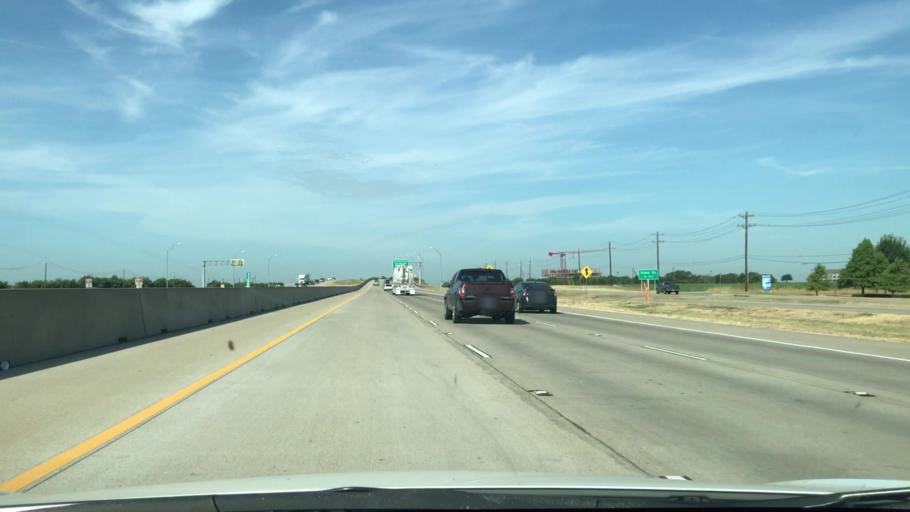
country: US
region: Texas
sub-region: Collin County
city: Allen
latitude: 33.1367
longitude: -96.7005
